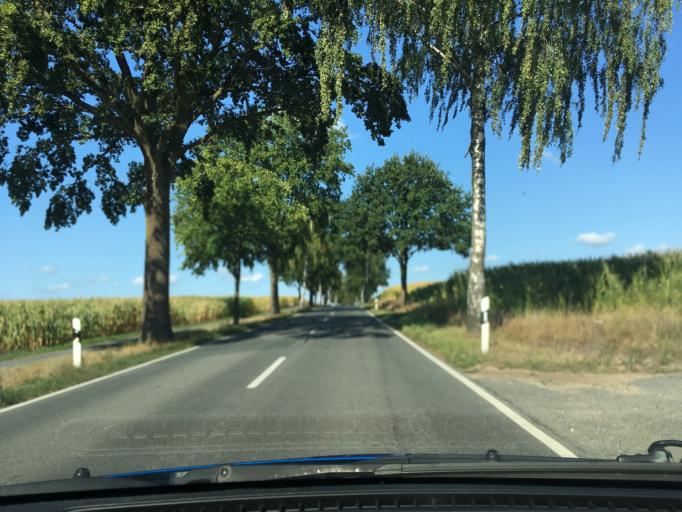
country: DE
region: Lower Saxony
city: Hermannsburg
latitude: 52.8476
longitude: 10.0740
